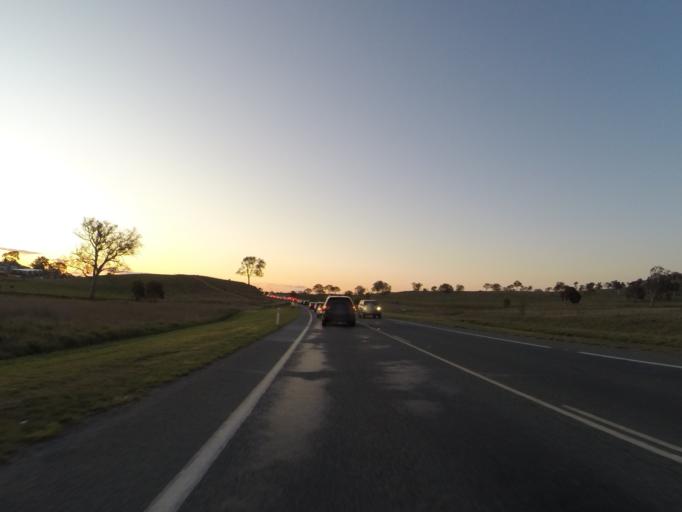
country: AU
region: Australian Capital Territory
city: Kaleen
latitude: -35.2032
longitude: 149.1686
